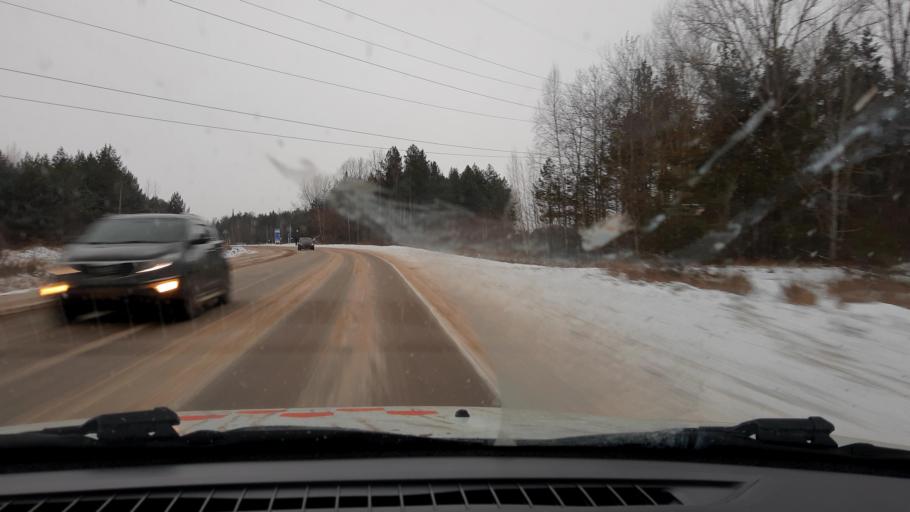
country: RU
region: Nizjnij Novgorod
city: Bor
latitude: 56.3238
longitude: 44.1448
